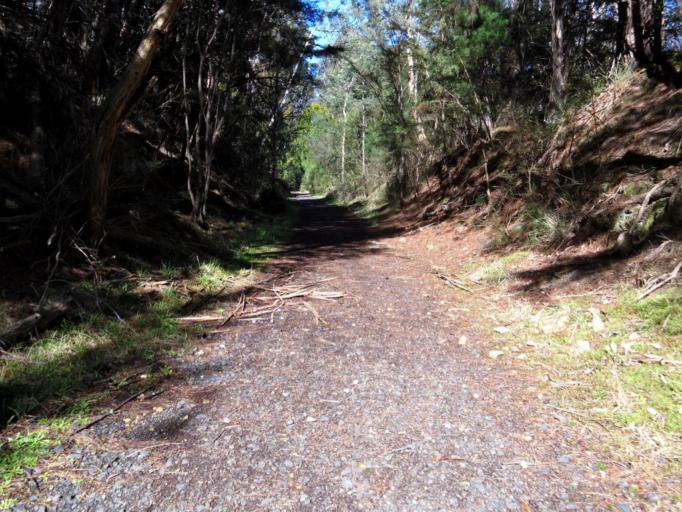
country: AU
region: Victoria
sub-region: Baw Baw
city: Warragul
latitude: -38.0713
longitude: 145.9219
